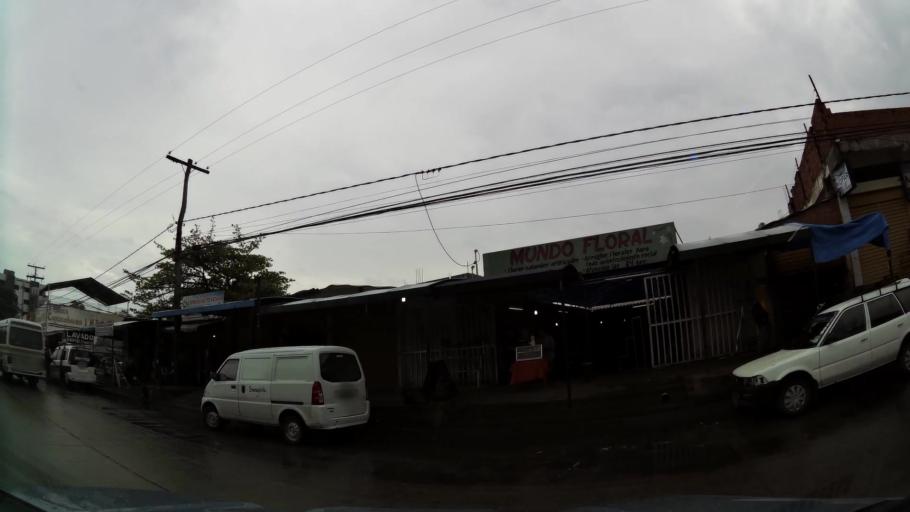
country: BO
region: Santa Cruz
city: Santa Cruz de la Sierra
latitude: -17.7922
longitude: -63.1629
